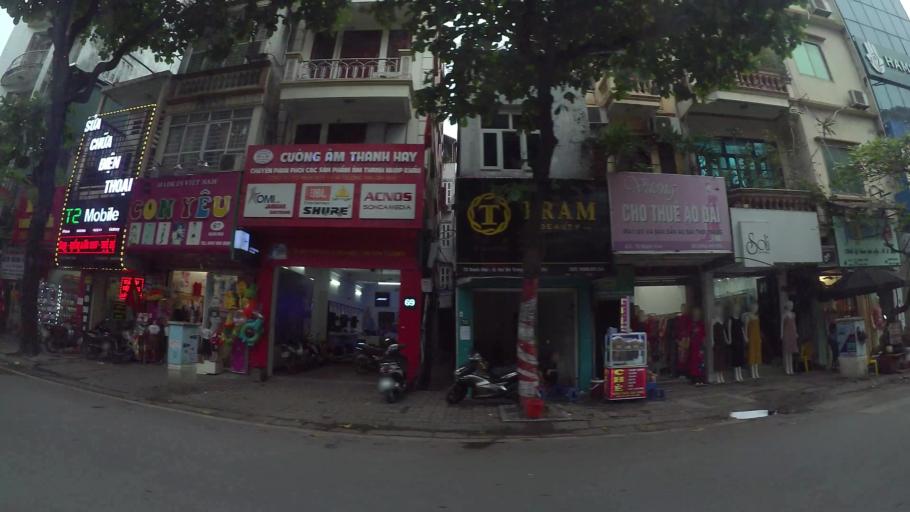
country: VN
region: Ha Noi
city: Hai BaTrung
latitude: 21.0074
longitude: 105.8513
